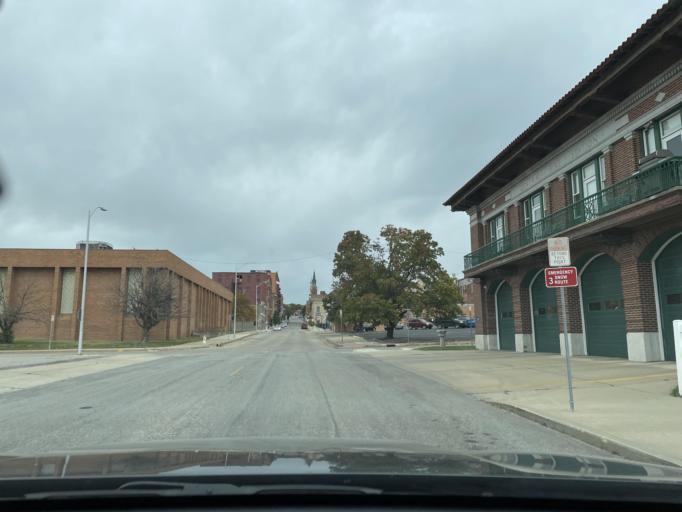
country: US
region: Missouri
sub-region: Buchanan County
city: Saint Joseph
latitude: 39.7638
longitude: -94.8518
